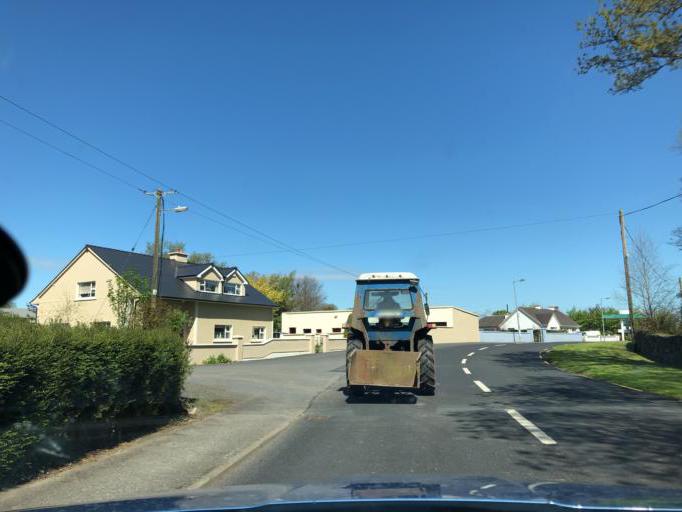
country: IE
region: Connaught
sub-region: County Galway
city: Portumna
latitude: 53.1468
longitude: -8.3718
